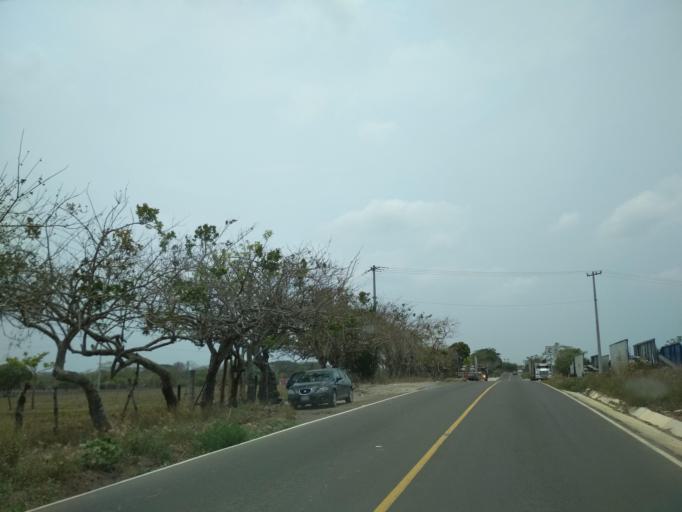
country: MX
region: Veracruz
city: Manlio Fabio Altamirano
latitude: 19.1370
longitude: -96.2987
